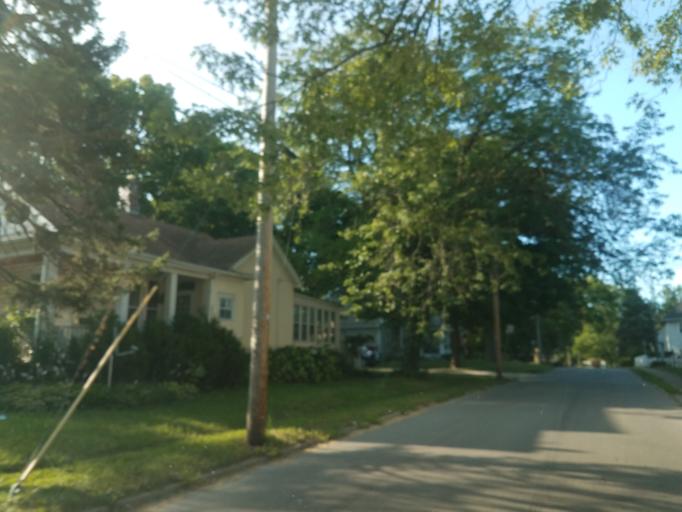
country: US
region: Illinois
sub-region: McLean County
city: Bloomington
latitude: 40.4781
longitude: -88.9780
